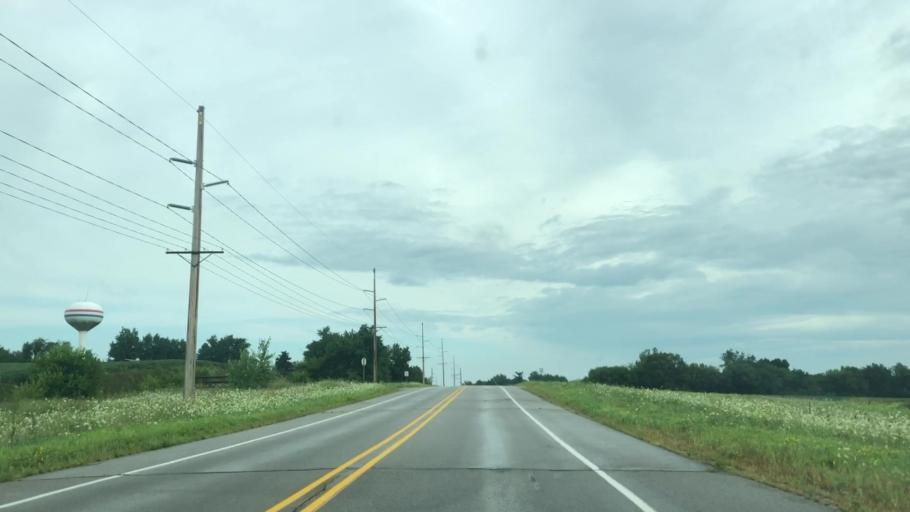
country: US
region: Iowa
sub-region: Marshall County
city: Marshalltown
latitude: 42.0283
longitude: -92.9604
